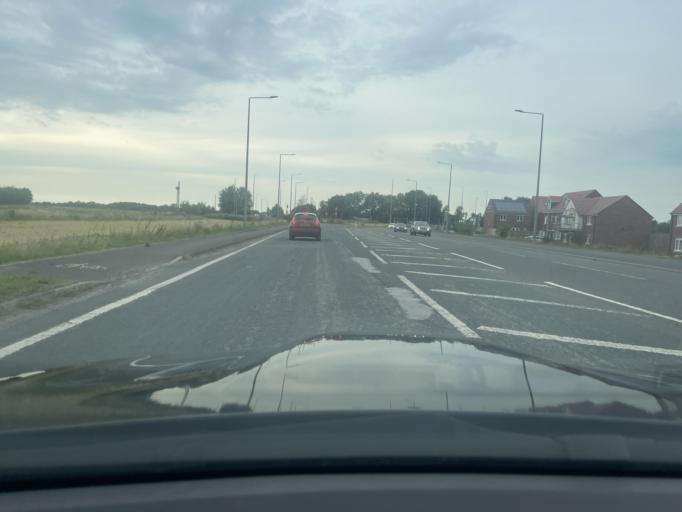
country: GB
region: England
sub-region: Lancashire
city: Leyland
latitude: 53.7118
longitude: -2.7161
